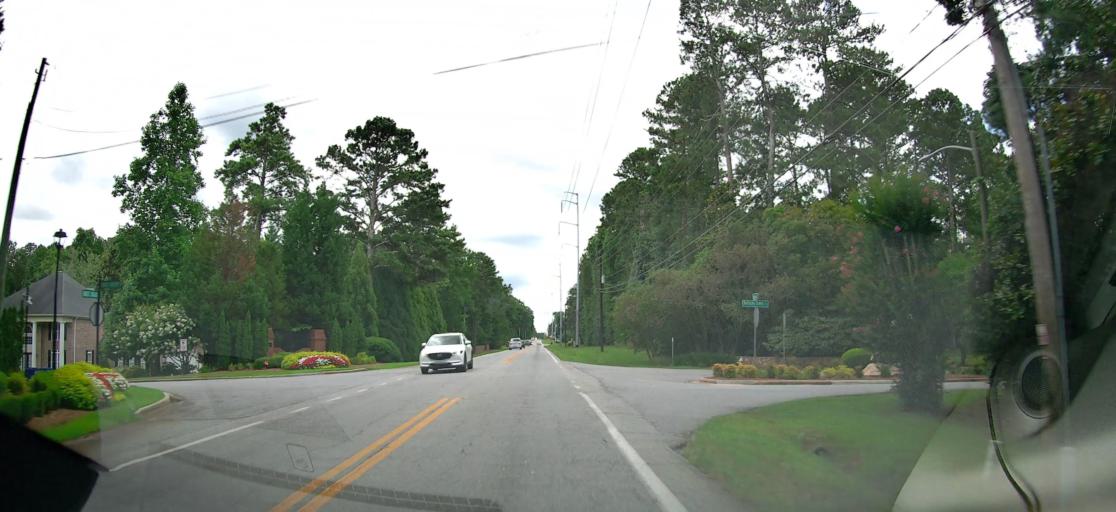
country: US
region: Georgia
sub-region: Bibb County
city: Macon
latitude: 32.9148
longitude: -83.7454
